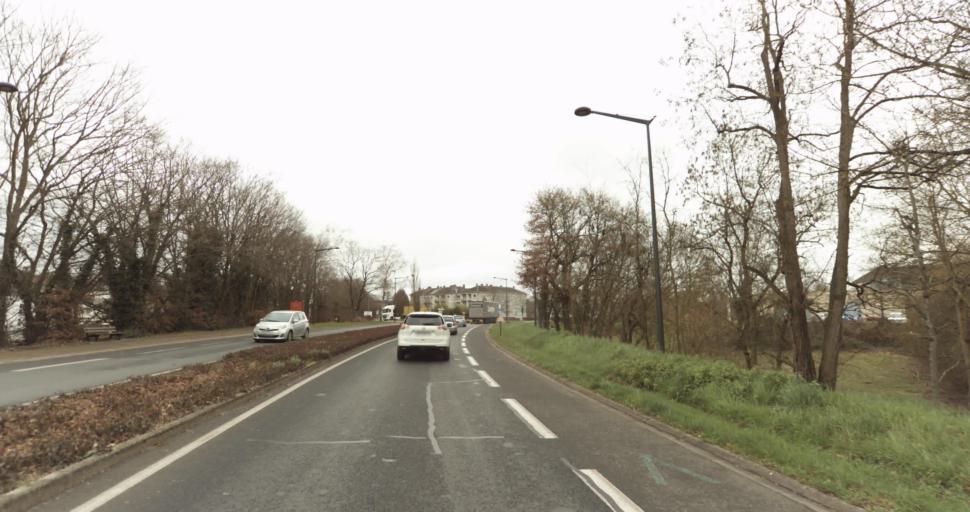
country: FR
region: Pays de la Loire
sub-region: Departement de Maine-et-Loire
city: Saumur
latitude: 47.2510
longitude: -0.0804
